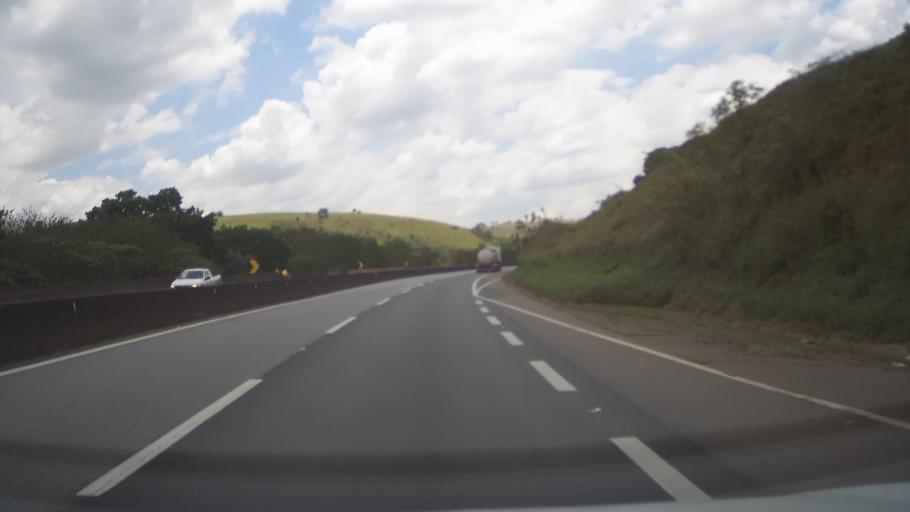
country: BR
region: Minas Gerais
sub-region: Tres Coracoes
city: Tres Coracoes
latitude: -21.7098
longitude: -45.3755
